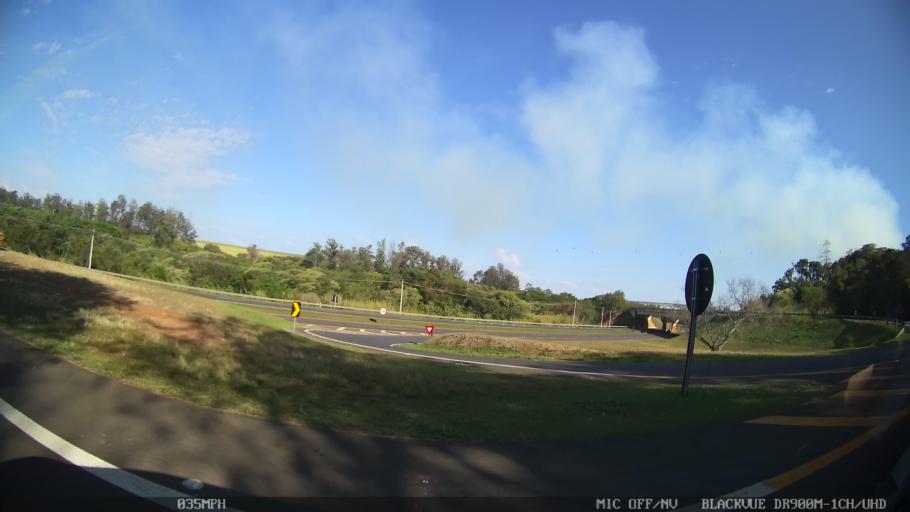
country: BR
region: Sao Paulo
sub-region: Piracicaba
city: Piracicaba
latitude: -22.6853
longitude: -47.5817
